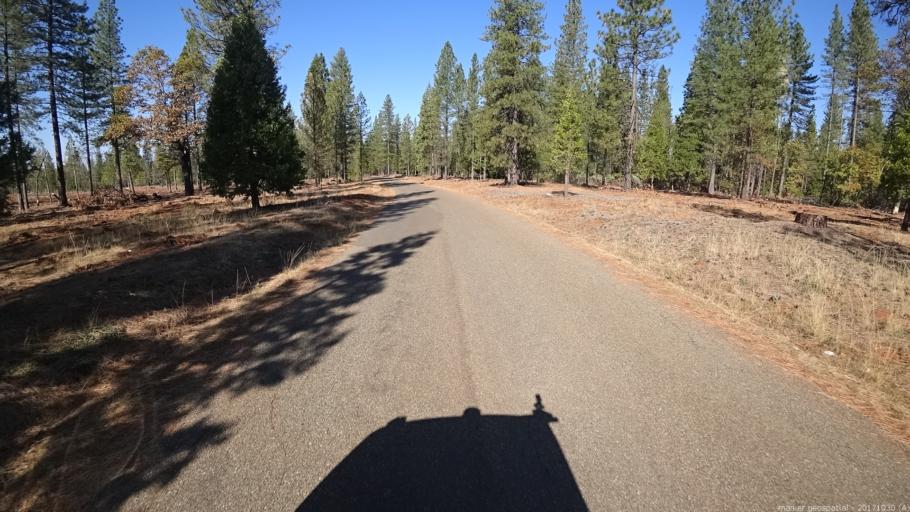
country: US
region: California
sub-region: Shasta County
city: Shingletown
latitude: 40.6130
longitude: -121.8793
